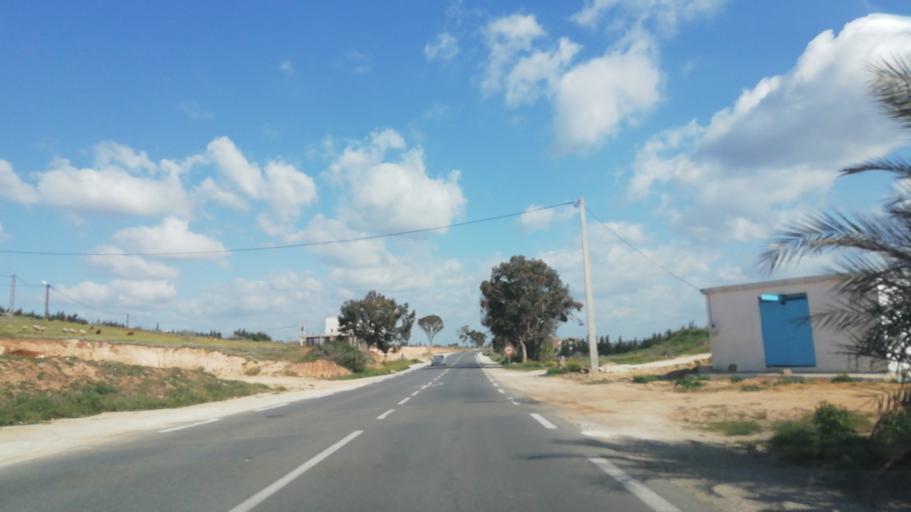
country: DZ
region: Relizane
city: Relizane
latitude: 35.7197
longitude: 0.3165
